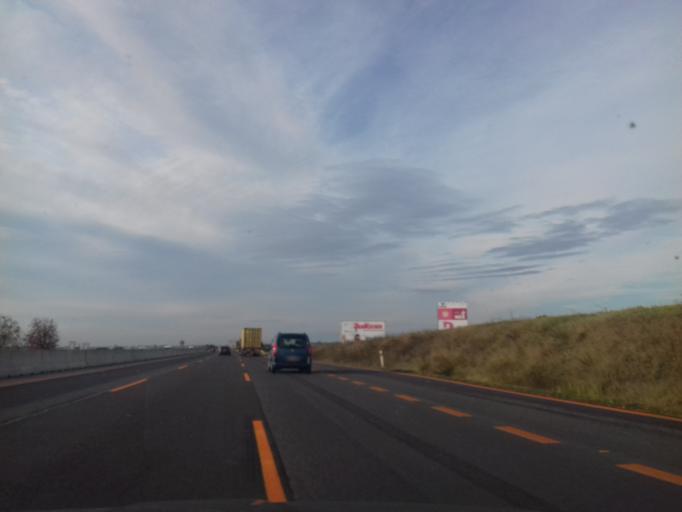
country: SK
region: Bratislavsky
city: Senec
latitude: 48.2364
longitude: 17.3660
